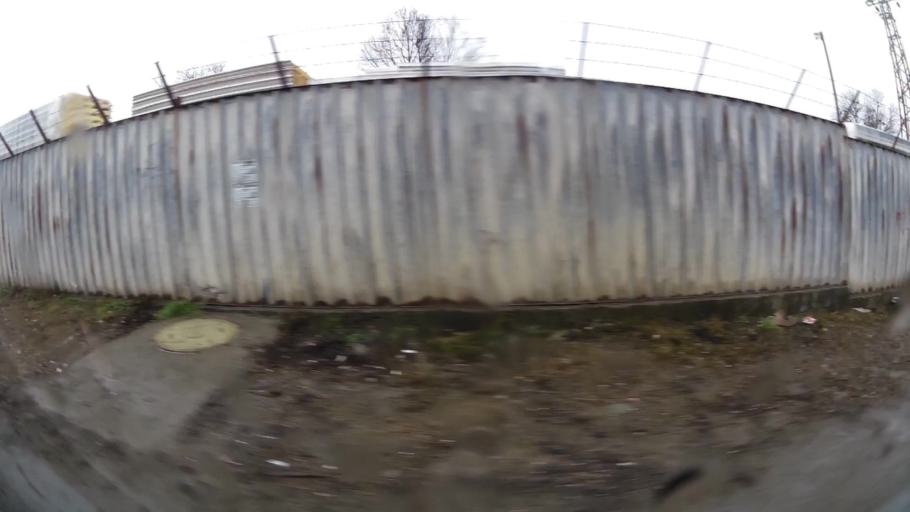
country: BG
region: Sofia-Capital
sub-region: Stolichna Obshtina
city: Sofia
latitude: 42.6574
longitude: 23.4265
